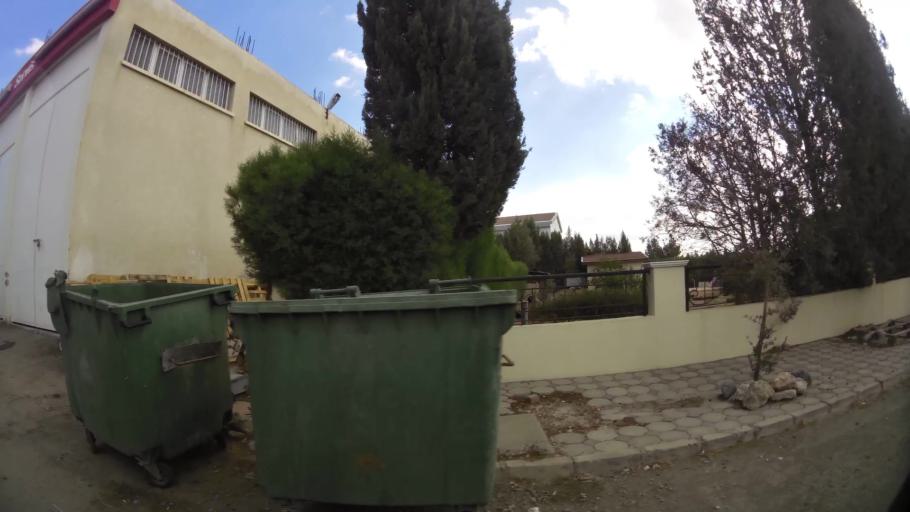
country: CY
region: Lefkosia
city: Nicosia
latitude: 35.2117
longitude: 33.3818
